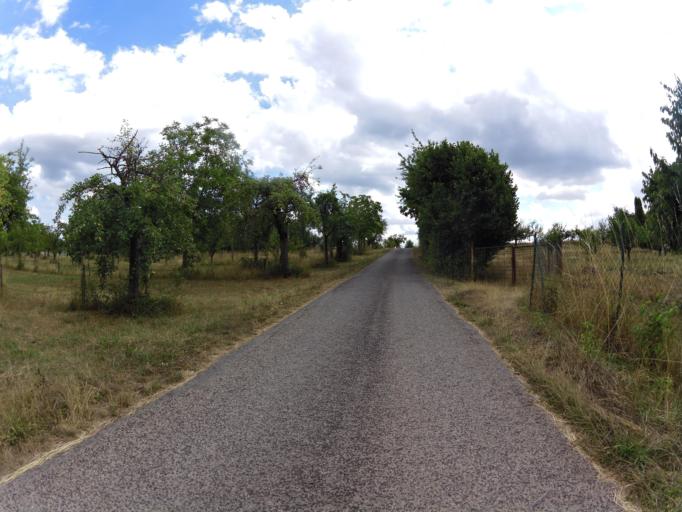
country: DE
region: Bavaria
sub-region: Regierungsbezirk Unterfranken
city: Zellingen
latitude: 49.8841
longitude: 9.8291
